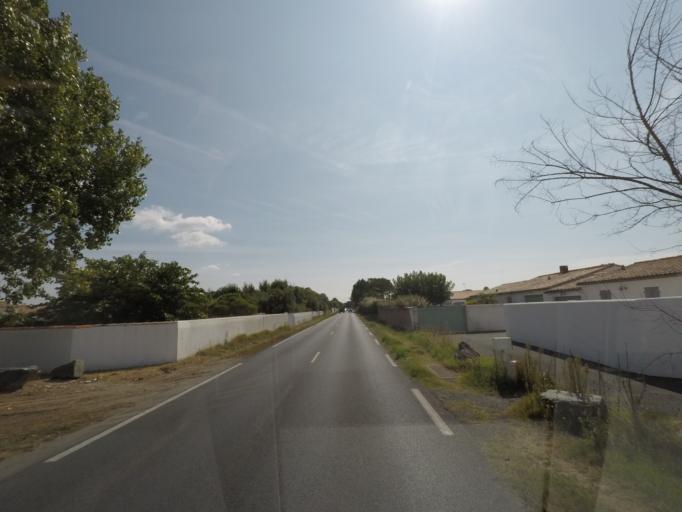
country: FR
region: Poitou-Charentes
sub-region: Departement de la Charente-Maritime
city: La Couarde-sur-Mer
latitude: 46.1979
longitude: -1.4363
